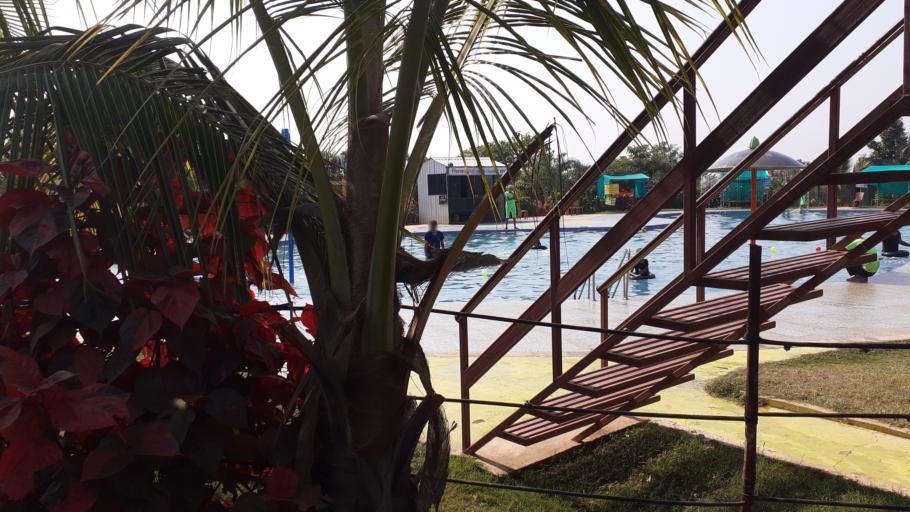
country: IN
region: Maharashtra
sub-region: Nagpur Division
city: Saoner
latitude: 21.4341
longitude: 78.8116
